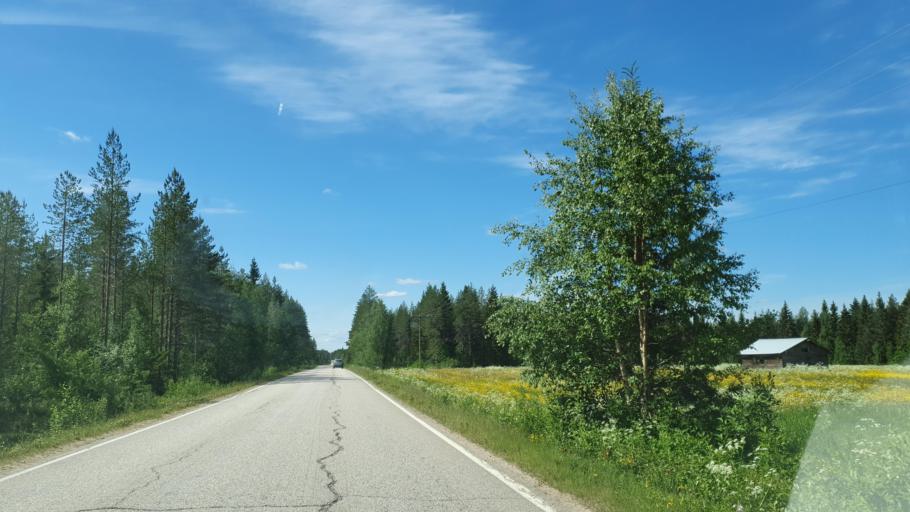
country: FI
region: Kainuu
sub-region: Kehys-Kainuu
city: Suomussalmi
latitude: 64.5869
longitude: 29.0641
